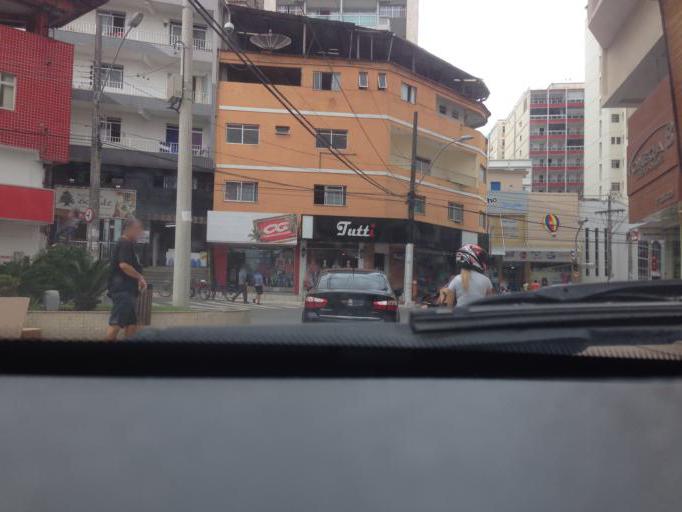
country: BR
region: Espirito Santo
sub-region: Guarapari
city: Guarapari
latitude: -20.6713
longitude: -40.4987
